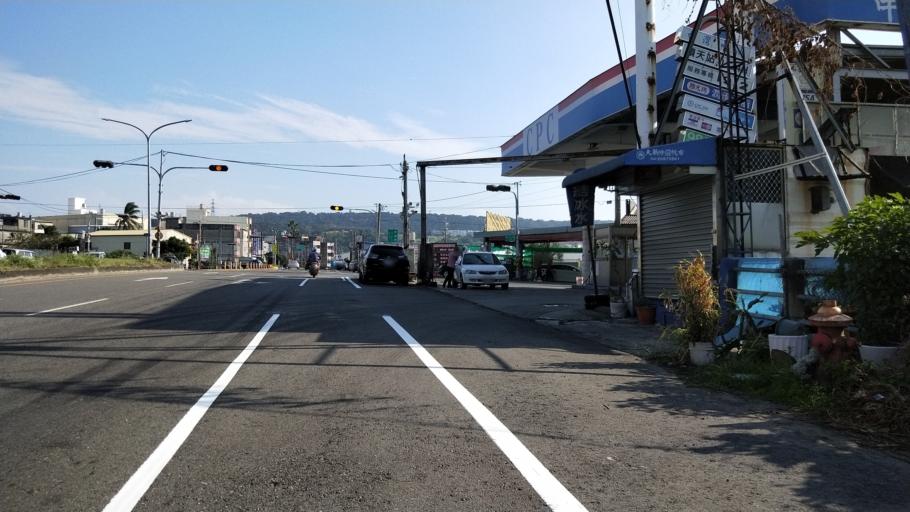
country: TW
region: Taiwan
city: Fengyuan
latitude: 24.3423
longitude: 120.6177
